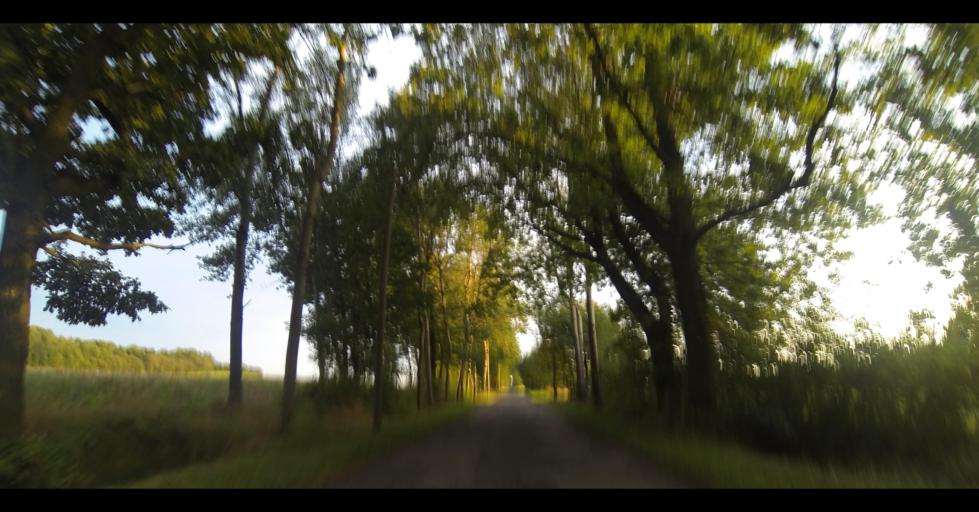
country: DE
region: Saxony
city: Albertstadt
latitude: 51.1318
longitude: 13.7553
